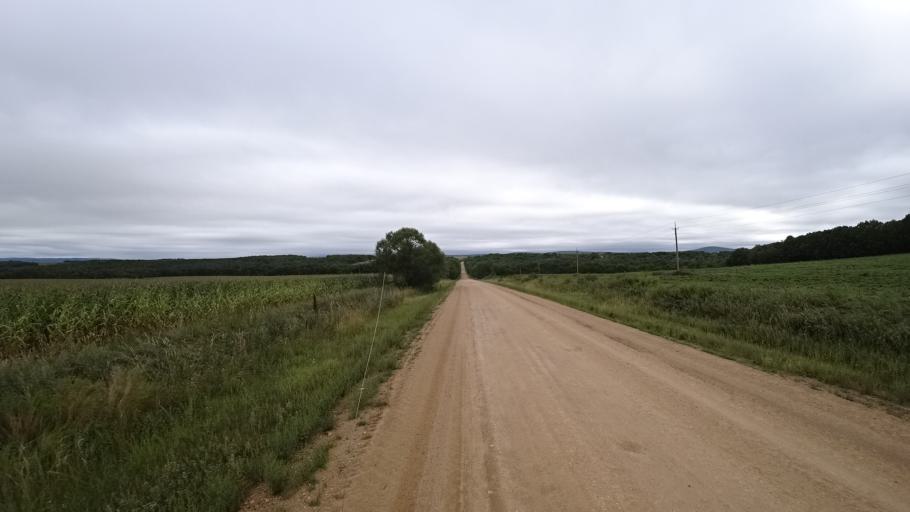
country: RU
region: Primorskiy
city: Monastyrishche
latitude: 44.0904
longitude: 132.5985
